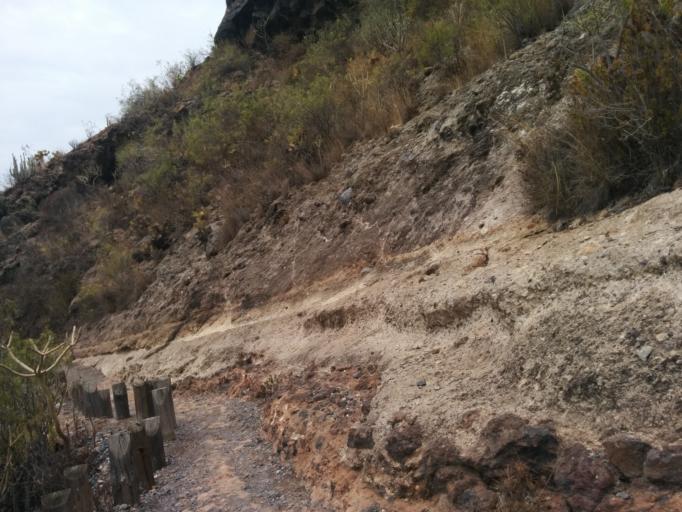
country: ES
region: Canary Islands
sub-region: Provincia de Santa Cruz de Tenerife
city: Adeje
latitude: 28.1277
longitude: -16.7225
